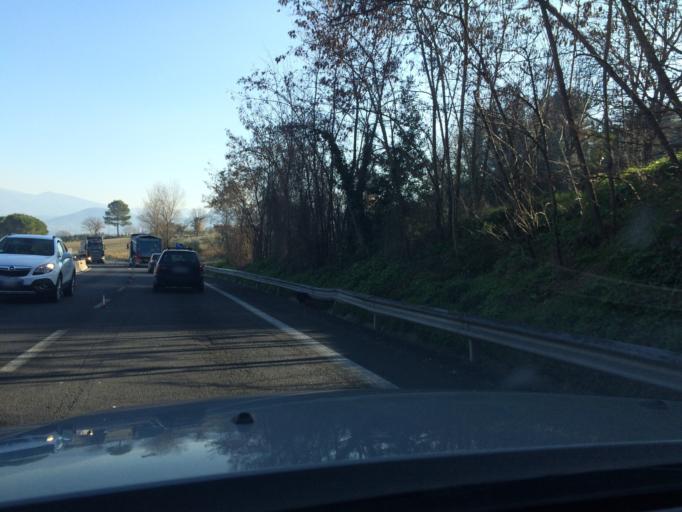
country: IT
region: Umbria
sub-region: Provincia di Terni
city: Narni Scalo
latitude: 42.5408
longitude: 12.5003
